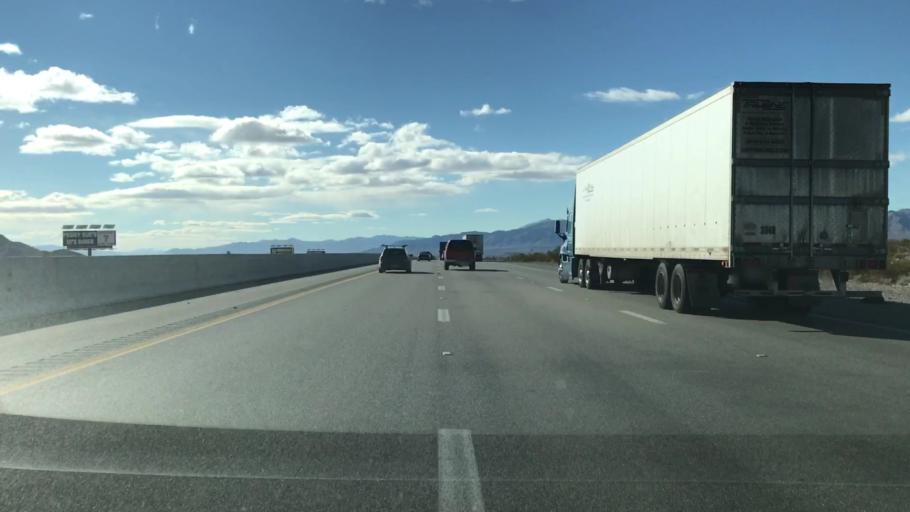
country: US
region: Nevada
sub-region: Clark County
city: Enterprise
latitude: 35.8173
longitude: -115.3020
